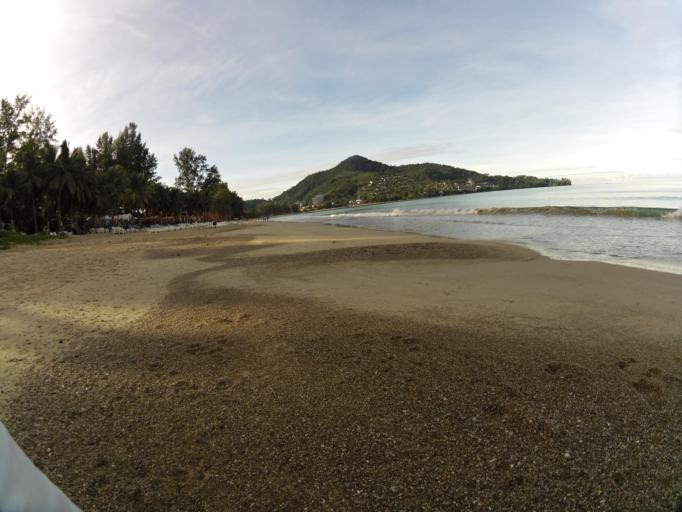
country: TH
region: Phuket
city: Patong
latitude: 7.9577
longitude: 98.2830
